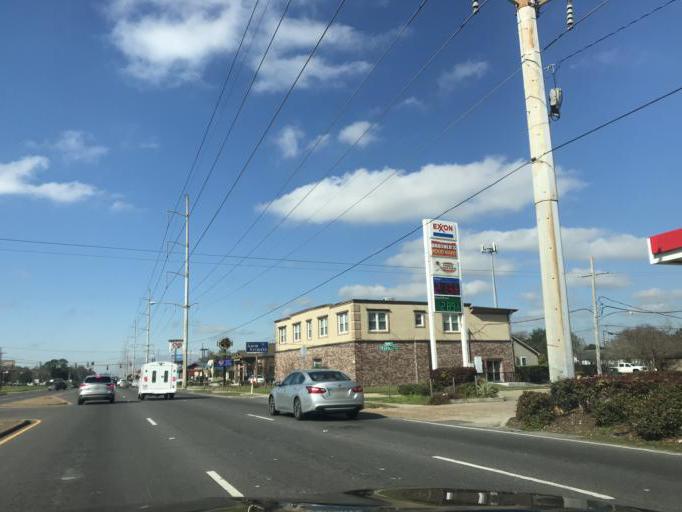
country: US
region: Louisiana
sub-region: Jefferson Parish
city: Metairie Terrace
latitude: 29.9754
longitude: -90.1732
